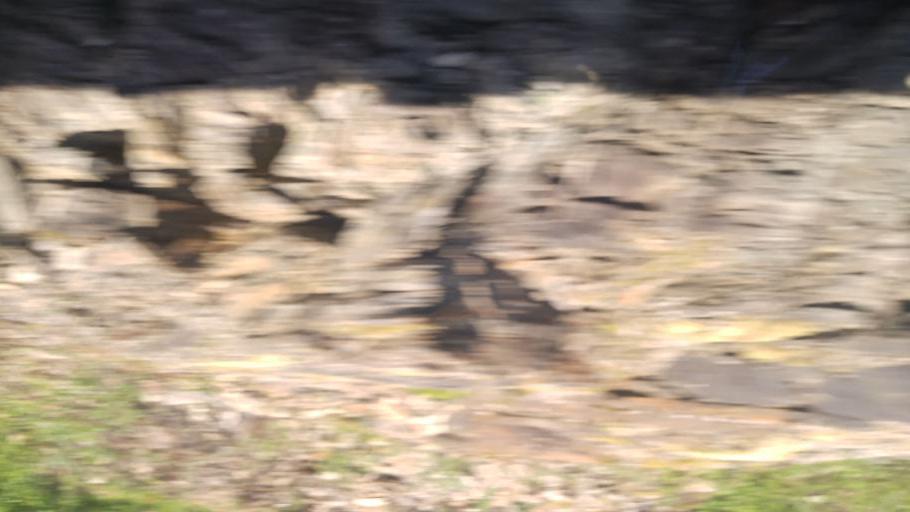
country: NO
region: Nord-Trondelag
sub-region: Meraker
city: Meraker
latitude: 63.3139
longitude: 12.1306
